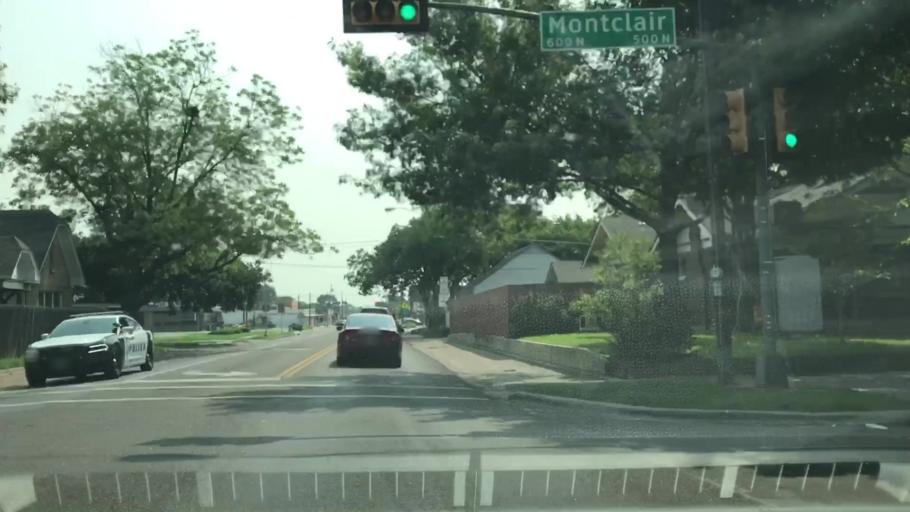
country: US
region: Texas
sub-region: Dallas County
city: Cockrell Hill
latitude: 32.7495
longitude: -96.8466
